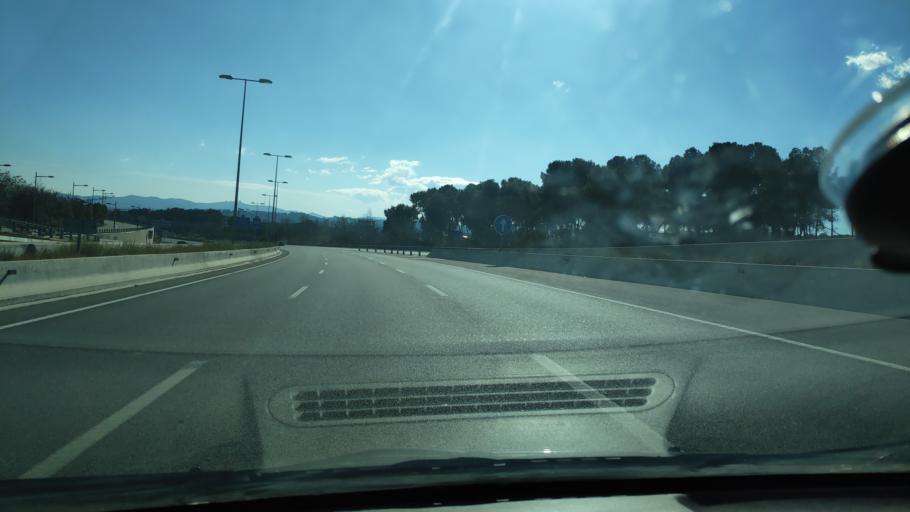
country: ES
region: Catalonia
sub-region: Provincia de Barcelona
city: Sant Quirze del Valles
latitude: 41.5496
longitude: 2.0755
